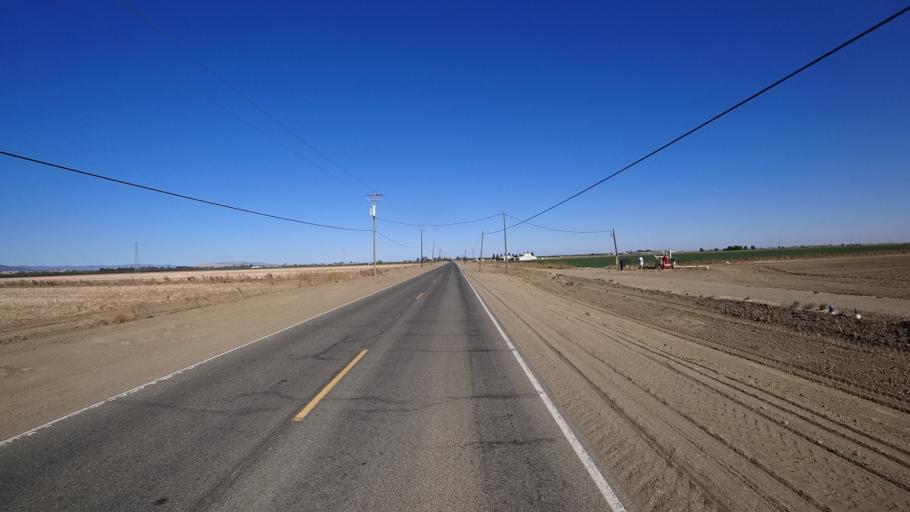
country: US
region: California
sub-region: Yolo County
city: Cottonwood
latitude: 38.6091
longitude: -121.9714
